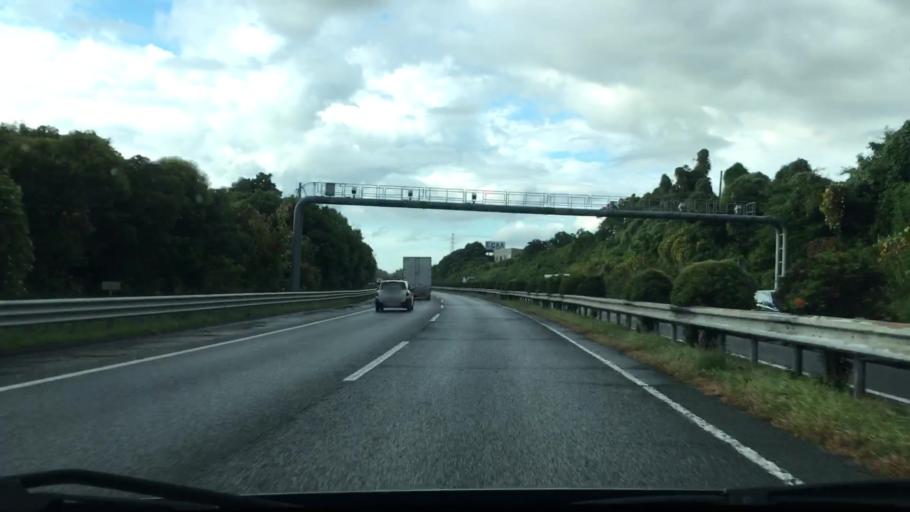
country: JP
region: Fukuoka
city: Koga
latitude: 33.6978
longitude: 130.4854
